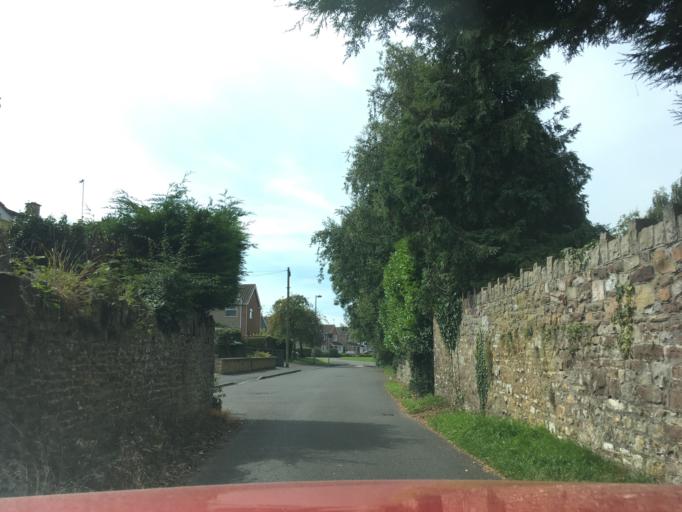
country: GB
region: England
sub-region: South Gloucestershire
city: Thornbury
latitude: 51.6166
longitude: -2.5170
